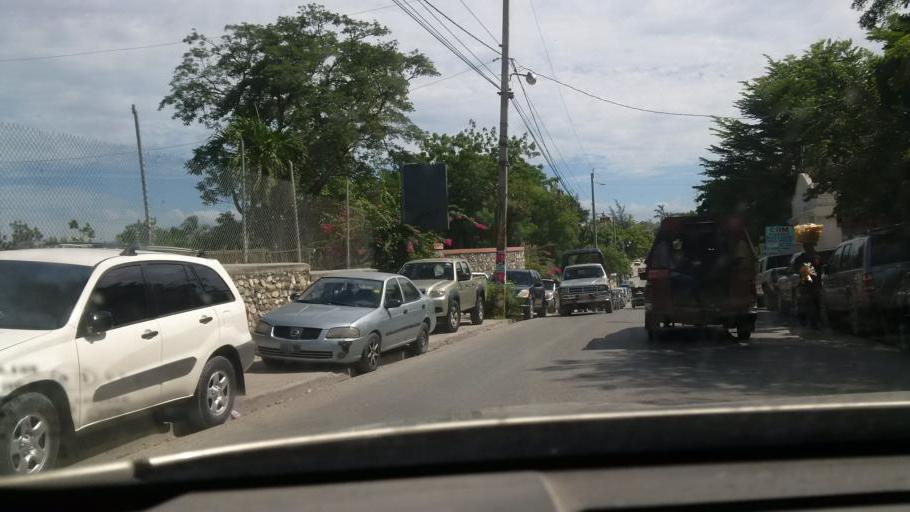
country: HT
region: Ouest
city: Delmas 73
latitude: 18.5547
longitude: -72.3007
